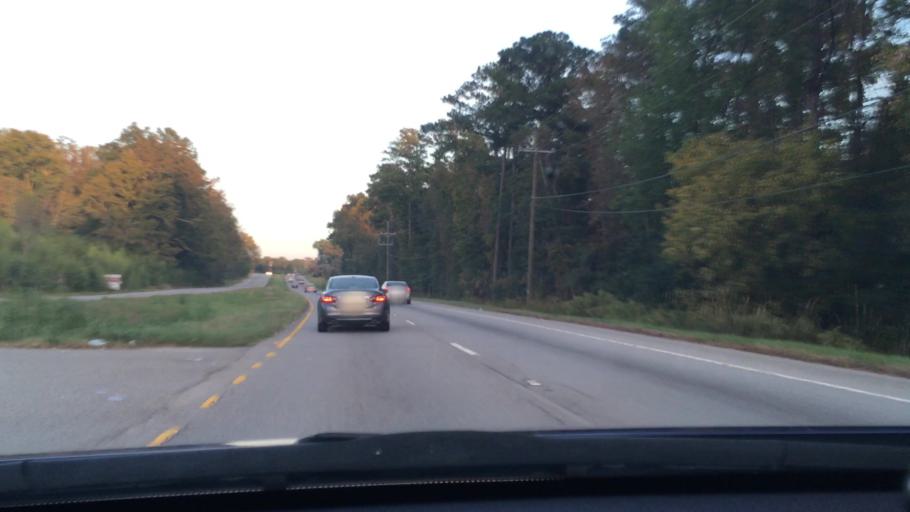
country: US
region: South Carolina
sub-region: Richland County
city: Hopkins
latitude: 33.9438
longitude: -80.8985
